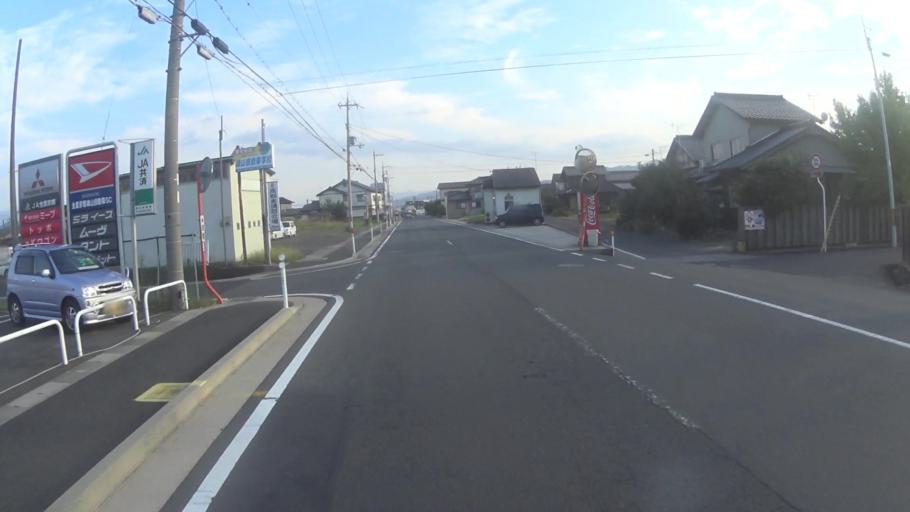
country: JP
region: Kyoto
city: Miyazu
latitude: 35.6223
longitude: 135.0740
